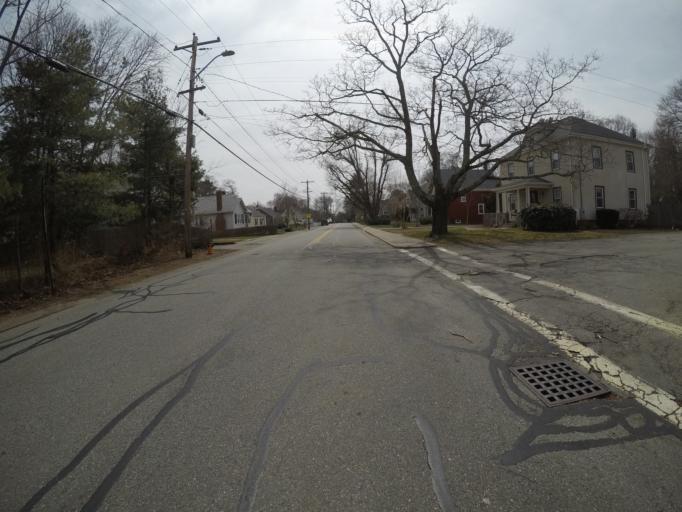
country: US
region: Massachusetts
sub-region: Bristol County
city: Easton
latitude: 42.0613
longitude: -71.1067
